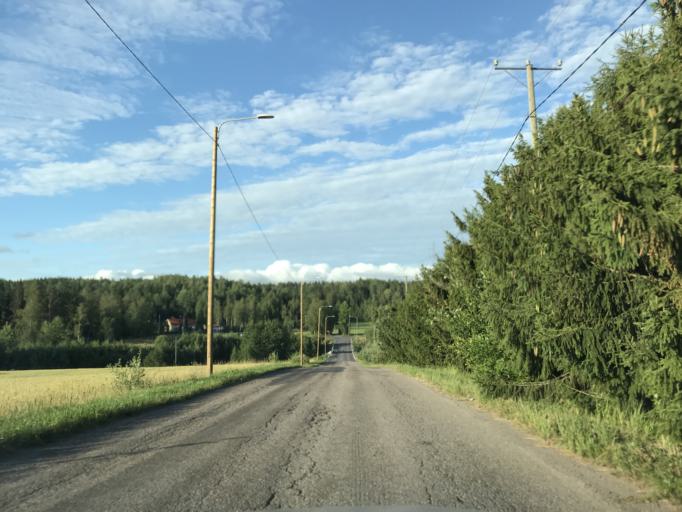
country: FI
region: Uusimaa
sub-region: Helsinki
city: Kauniainen
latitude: 60.3596
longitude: 24.6867
